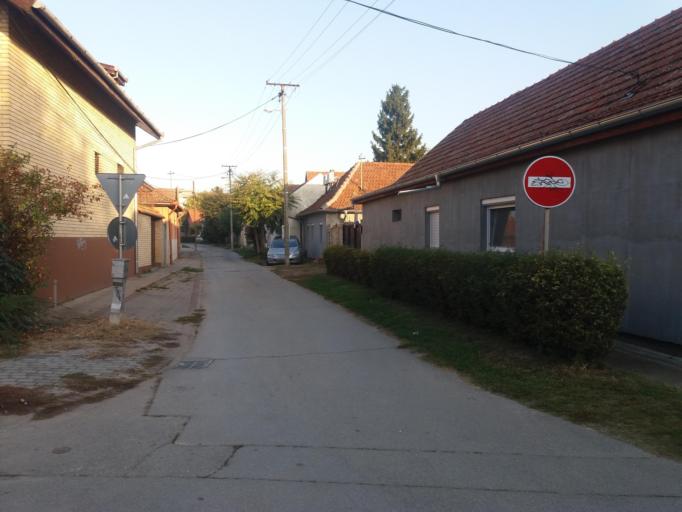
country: RS
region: Autonomna Pokrajina Vojvodina
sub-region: Severnobacki Okrug
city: Subotica
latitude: 46.0930
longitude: 19.6739
